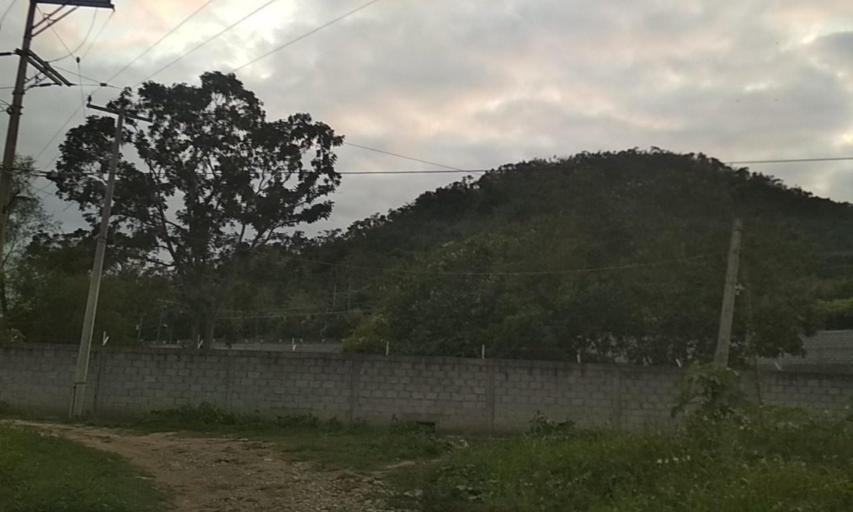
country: MX
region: Veracruz
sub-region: Papantla
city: El Chote
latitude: 20.4223
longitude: -97.3343
